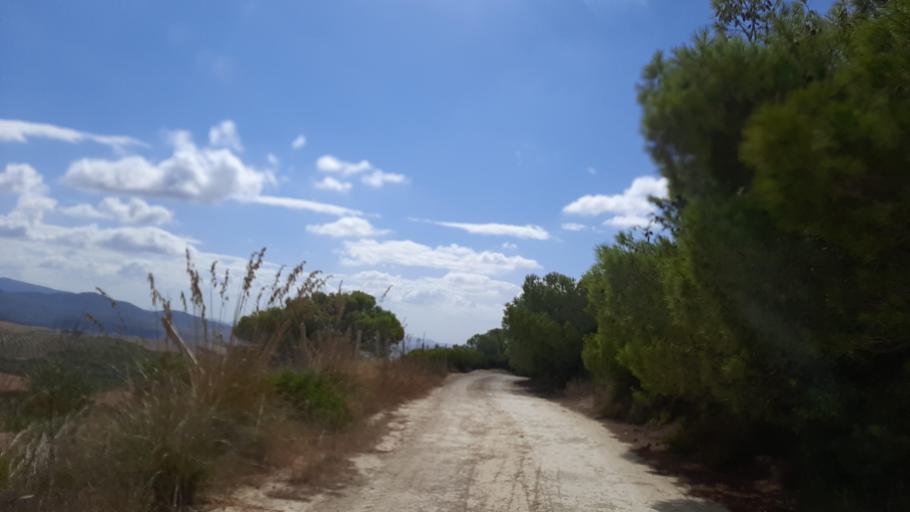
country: TN
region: Zaghwan
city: Zaghouan
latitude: 36.4930
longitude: 10.1758
